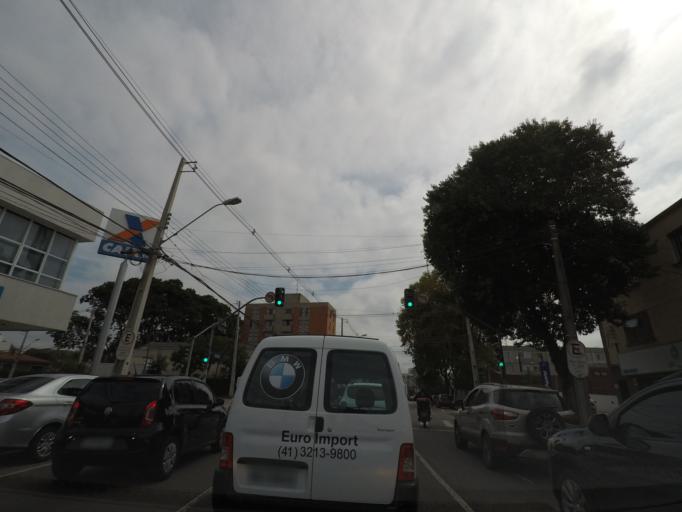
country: BR
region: Parana
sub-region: Curitiba
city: Curitiba
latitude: -25.4535
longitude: -49.2765
